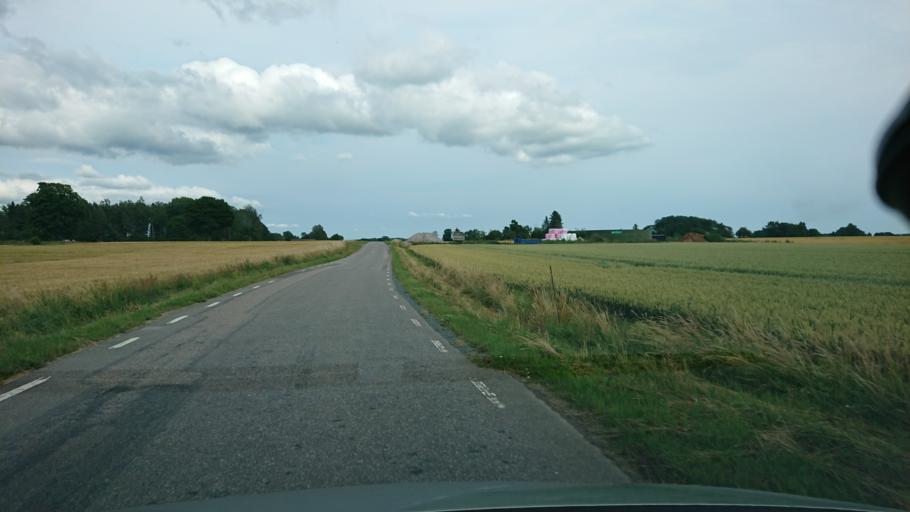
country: SE
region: Uppsala
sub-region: Osthammars Kommun
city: Bjorklinge
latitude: 59.9903
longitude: 17.5190
